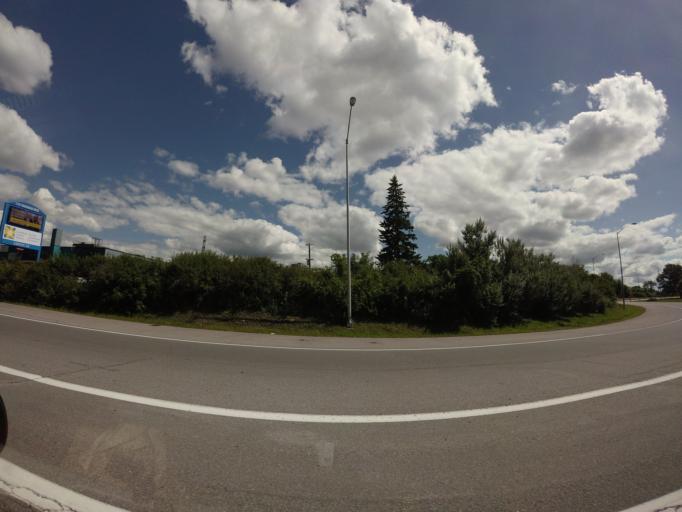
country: CA
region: Ontario
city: Ottawa
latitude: 45.3719
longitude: -75.7528
